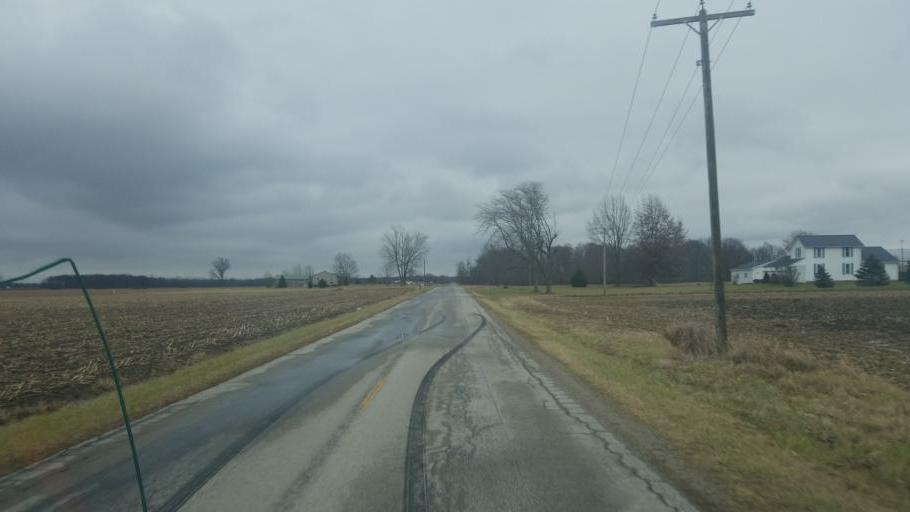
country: US
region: Ohio
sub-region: Crawford County
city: Galion
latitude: 40.6755
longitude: -82.8873
